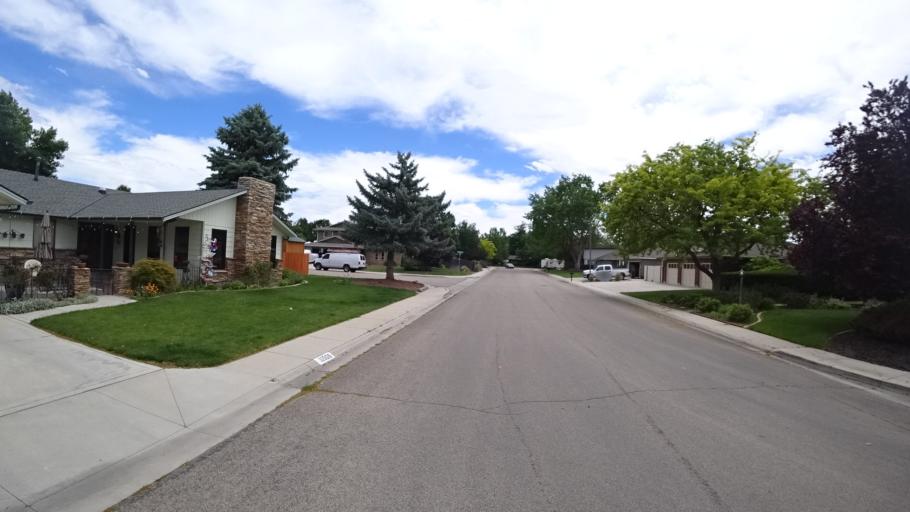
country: US
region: Idaho
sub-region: Ada County
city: Eagle
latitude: 43.6350
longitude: -116.3258
